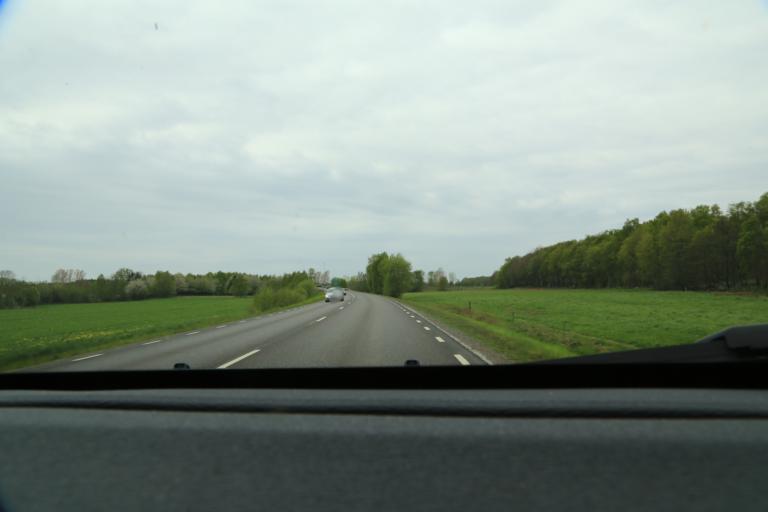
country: SE
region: Halland
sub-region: Varbergs Kommun
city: Tvaaker
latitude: 57.0486
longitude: 12.3736
